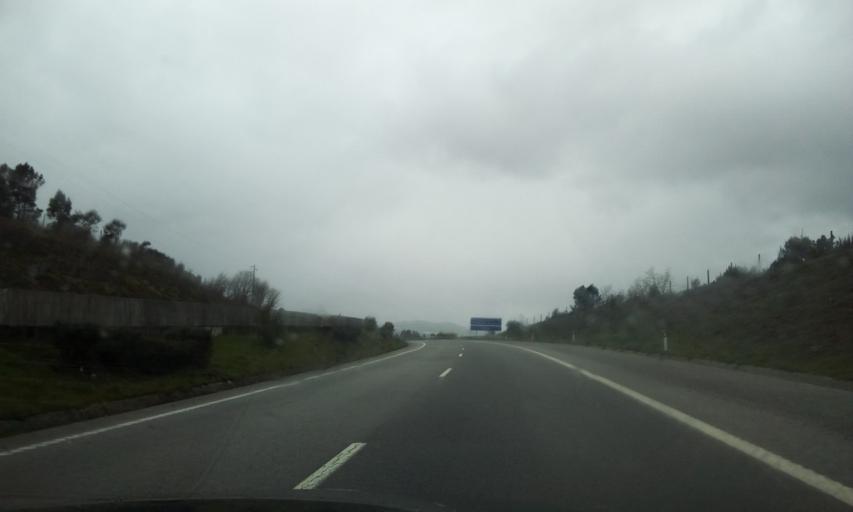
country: PT
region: Viseu
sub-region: Mangualde
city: Mangualde
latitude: 40.6147
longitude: -7.6597
